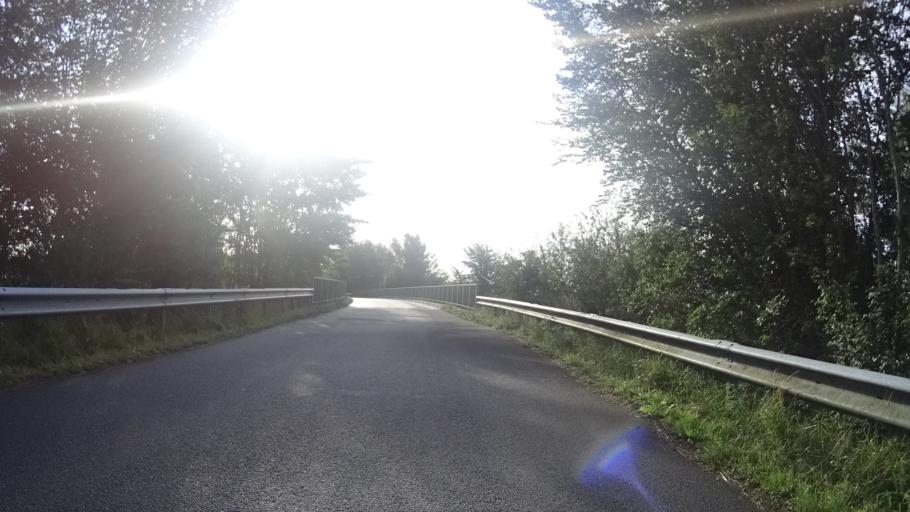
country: DE
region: Lower Saxony
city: Nordenham
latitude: 53.4935
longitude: 8.4560
